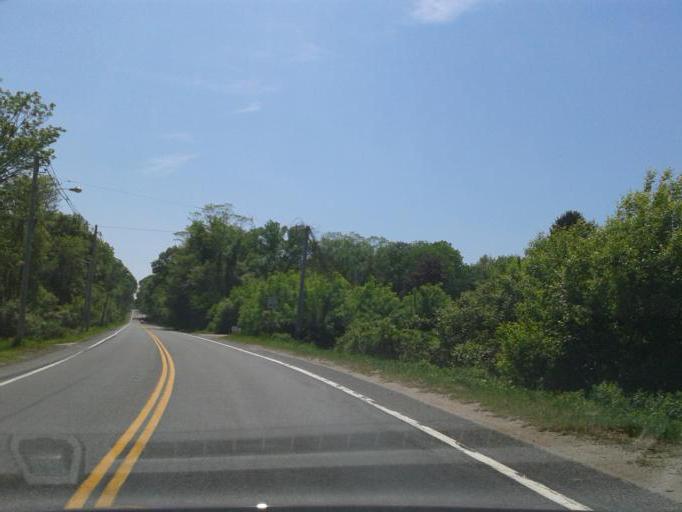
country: US
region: Rhode Island
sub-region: Washington County
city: Kingston
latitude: 41.4904
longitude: -71.4885
